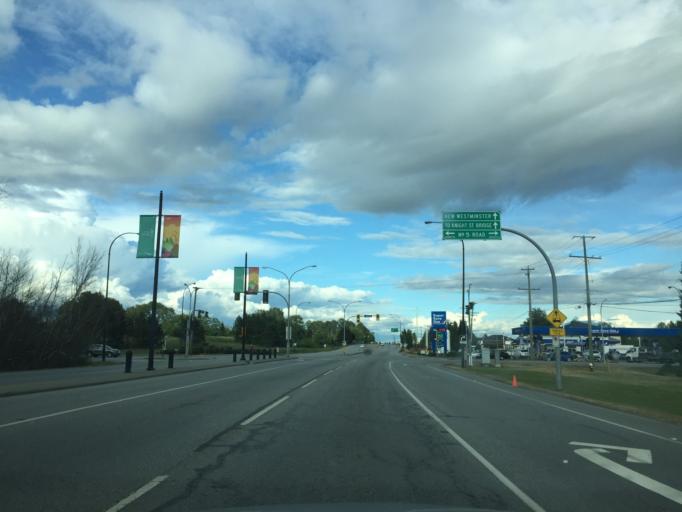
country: CA
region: British Columbia
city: Richmond
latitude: 49.1702
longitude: -123.0932
